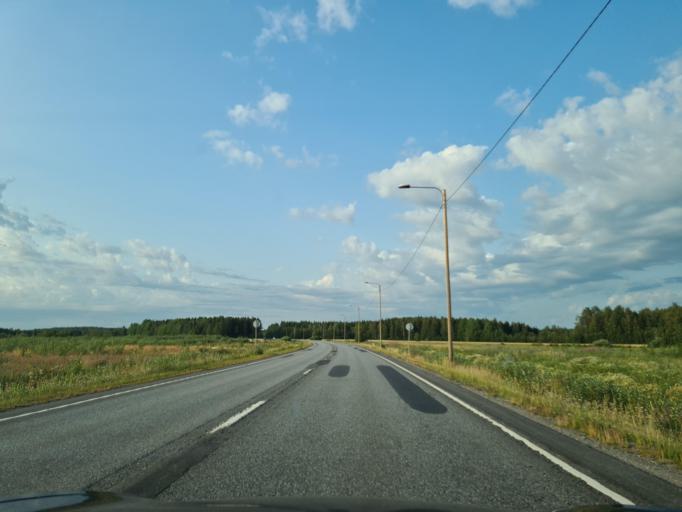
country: FI
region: Southern Ostrobothnia
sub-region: Seinaejoki
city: Kauhava
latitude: 63.0601
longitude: 23.0390
